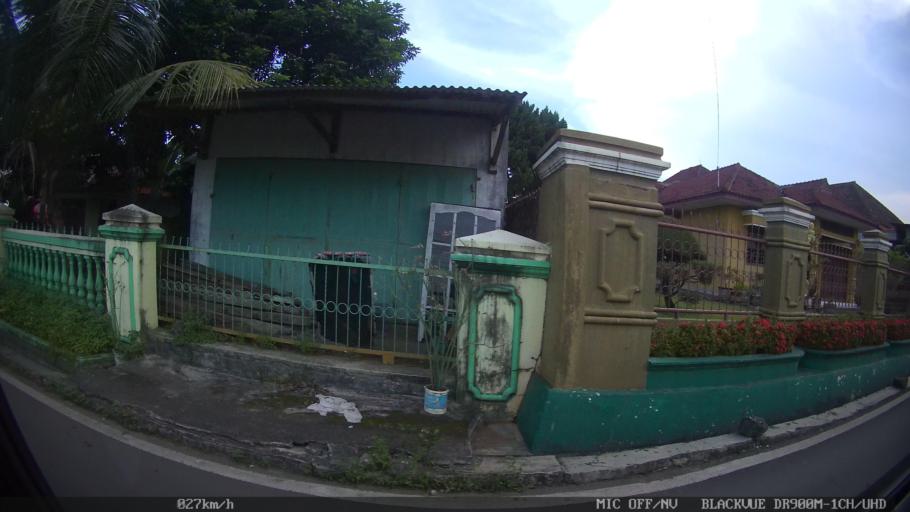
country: ID
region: Lampung
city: Kedaton
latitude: -5.3892
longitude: 105.2313
